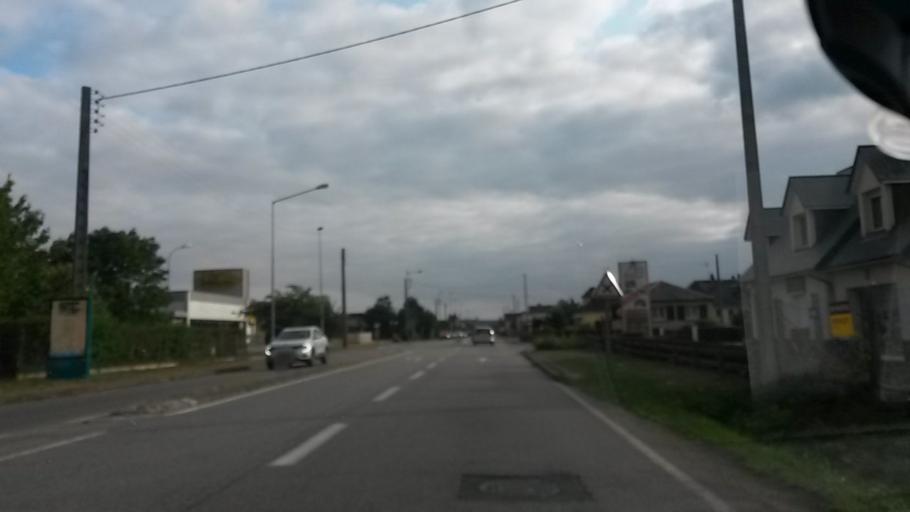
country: FR
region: Haute-Normandie
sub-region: Departement de l'Eure
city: Gravigny
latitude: 49.0554
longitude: 1.1674
